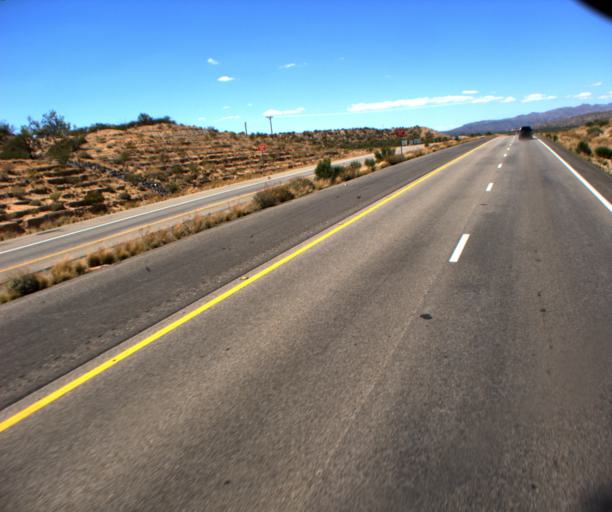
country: US
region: Arizona
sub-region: Yavapai County
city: Bagdad
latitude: 34.8127
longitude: -113.6260
